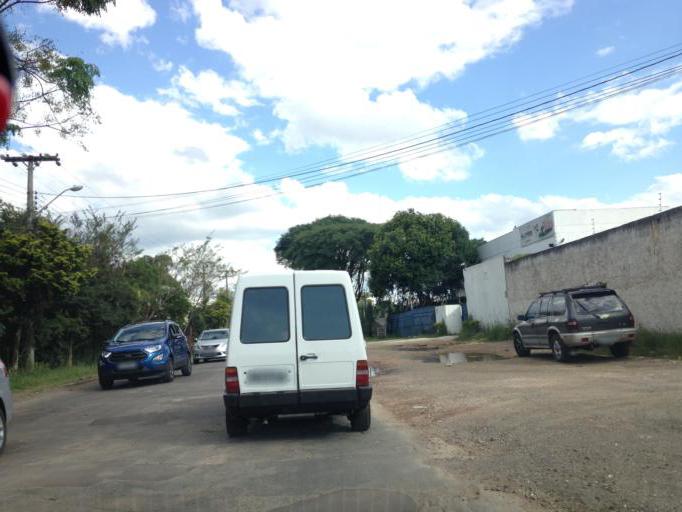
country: BR
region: Parana
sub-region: Pinhais
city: Pinhais
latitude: -25.4166
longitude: -49.2195
